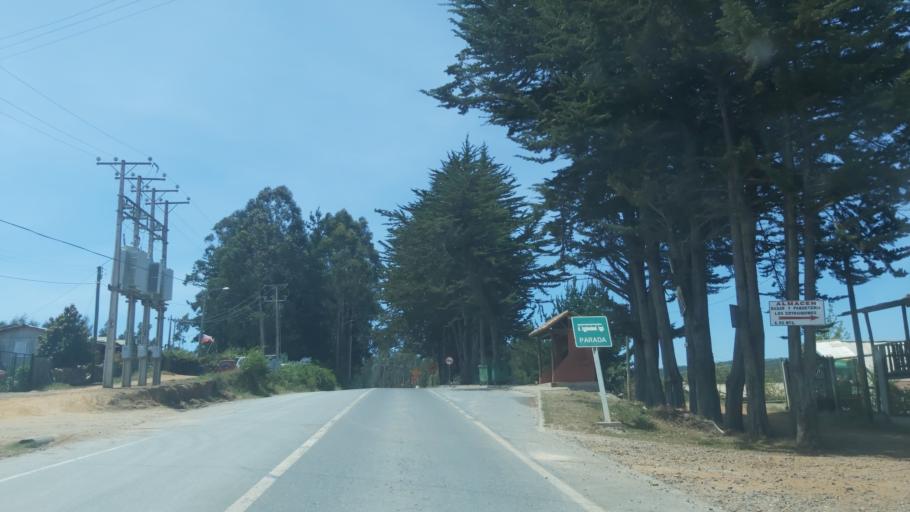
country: CL
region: Maule
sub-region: Provincia de Talca
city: Constitucion
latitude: -35.4413
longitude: -72.4574
